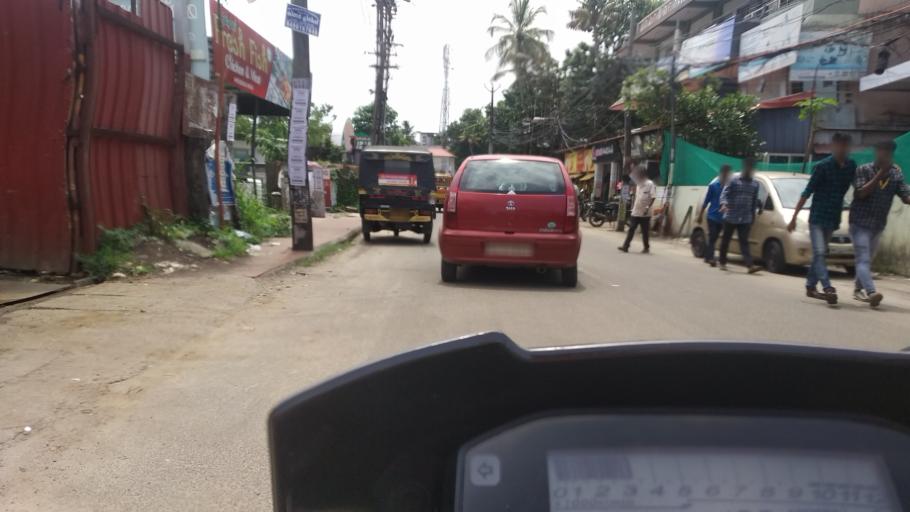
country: IN
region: Kerala
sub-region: Ernakulam
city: Cochin
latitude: 9.9910
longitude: 76.3096
